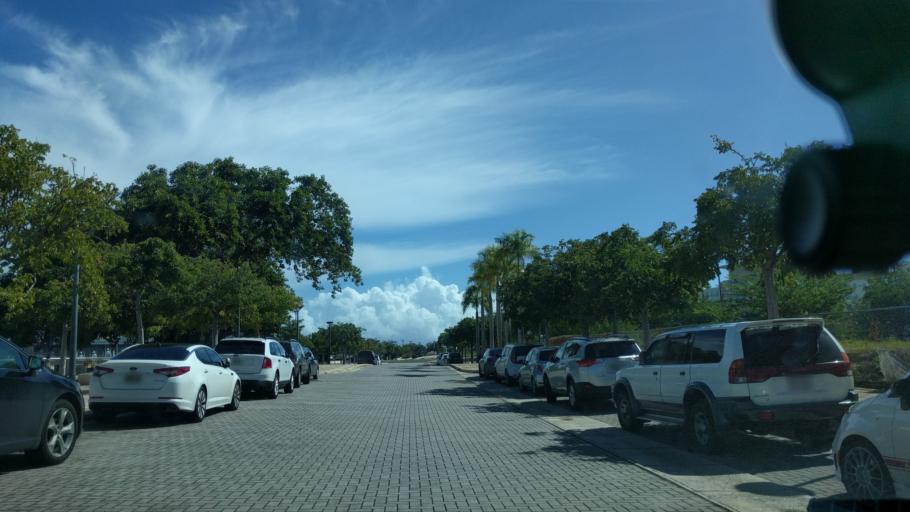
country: PR
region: San Juan
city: San Juan
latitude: 18.4558
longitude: -66.0899
